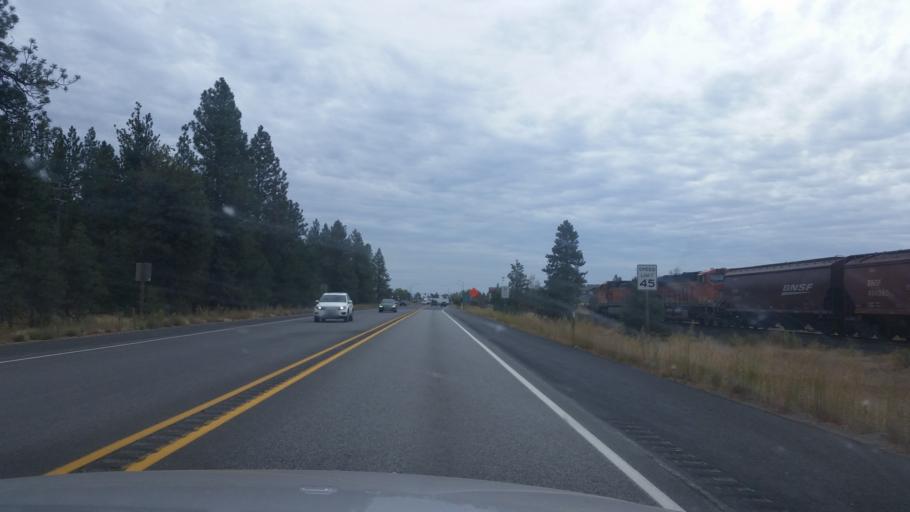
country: US
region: Washington
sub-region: Spokane County
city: Cheney
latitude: 47.5116
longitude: -117.5647
